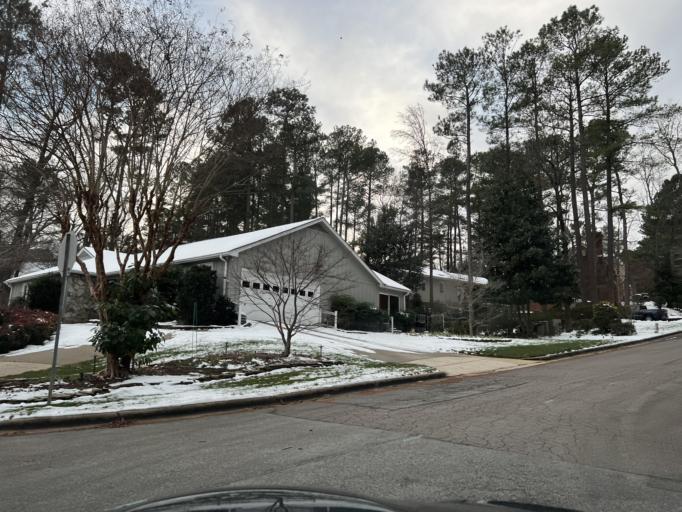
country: US
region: North Carolina
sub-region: Wake County
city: West Raleigh
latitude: 35.8731
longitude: -78.6017
